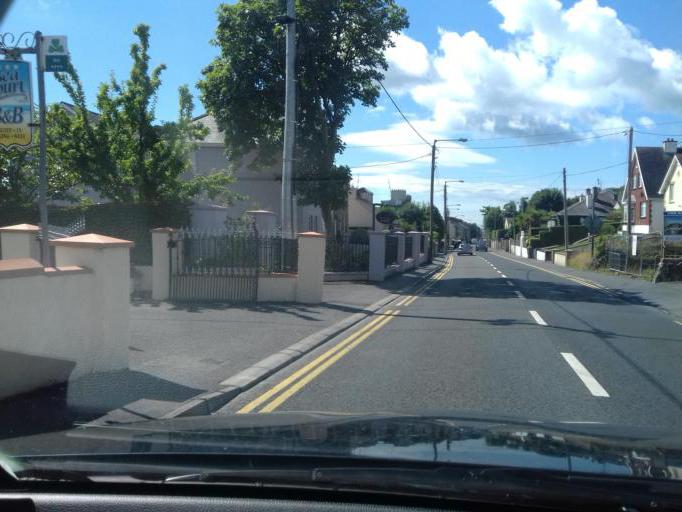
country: IE
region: Munster
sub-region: Waterford
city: Tra Mhor
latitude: 52.1674
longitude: -7.1444
